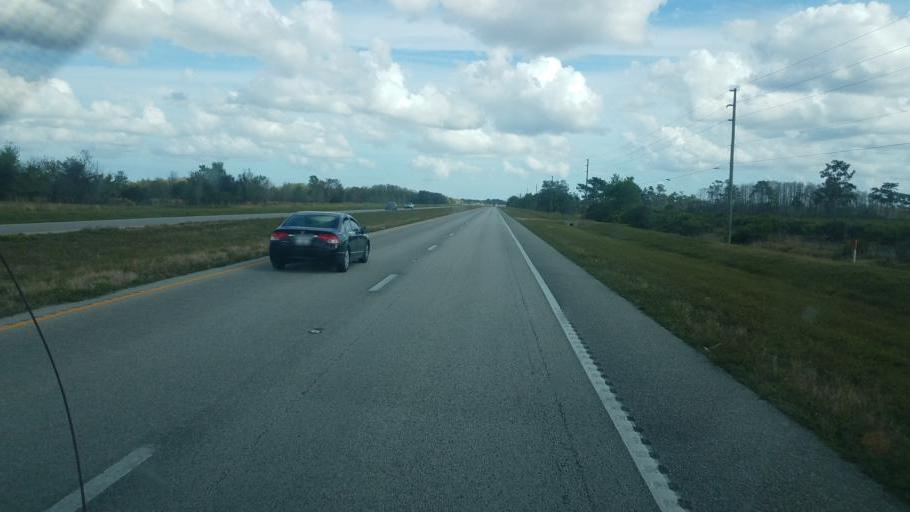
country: US
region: Florida
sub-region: Osceola County
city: Saint Cloud
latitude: 28.1295
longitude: -80.9955
